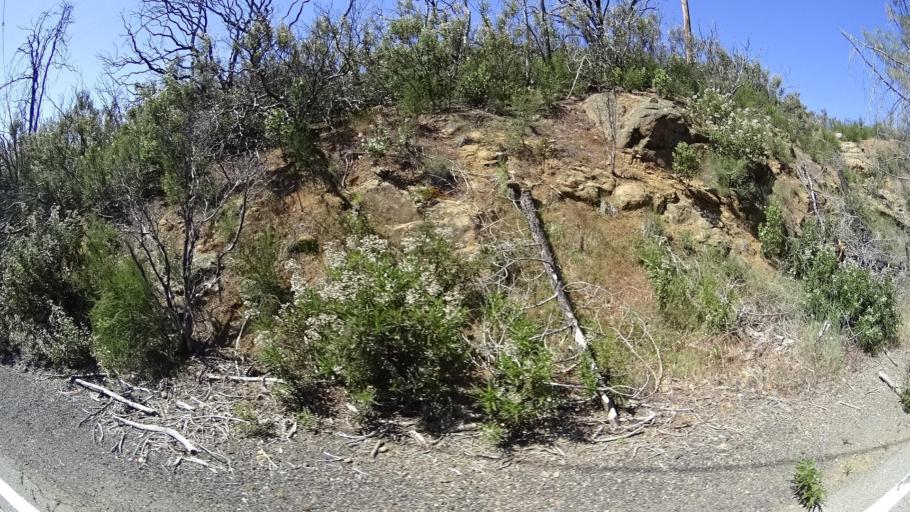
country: US
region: California
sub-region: Lake County
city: Hidden Valley Lake
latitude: 38.8813
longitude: -122.4494
